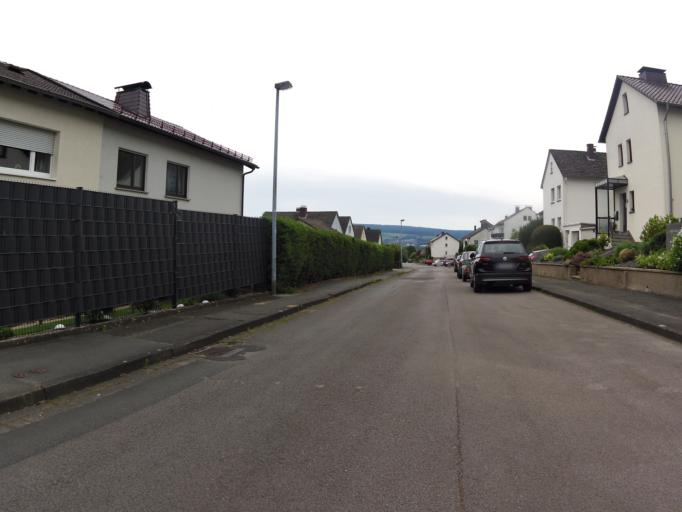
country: DE
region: North Rhine-Westphalia
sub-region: Regierungsbezirk Detmold
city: Hoexter
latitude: 51.7822
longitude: 9.3653
